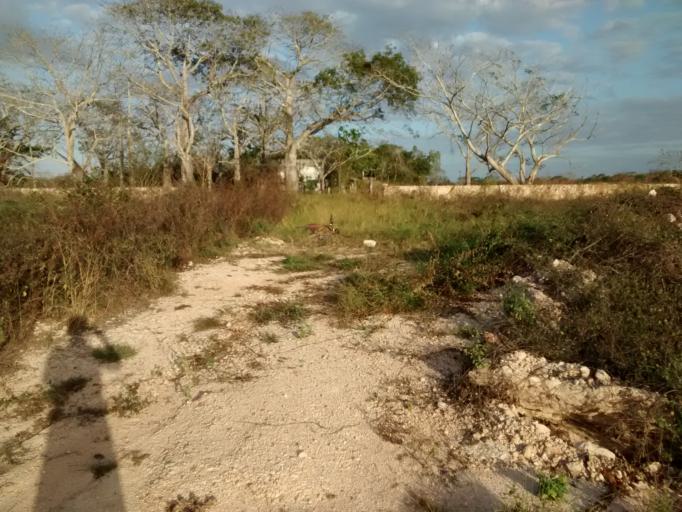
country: MX
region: Yucatan
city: Valladolid
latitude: 20.6790
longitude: -88.1723
